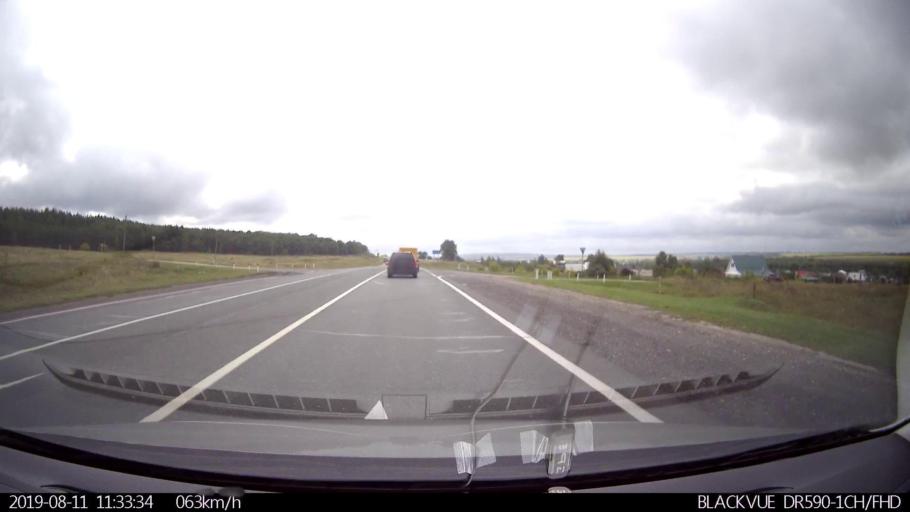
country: RU
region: Ulyanovsk
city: Silikatnyy
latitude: 54.0259
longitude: 48.2136
